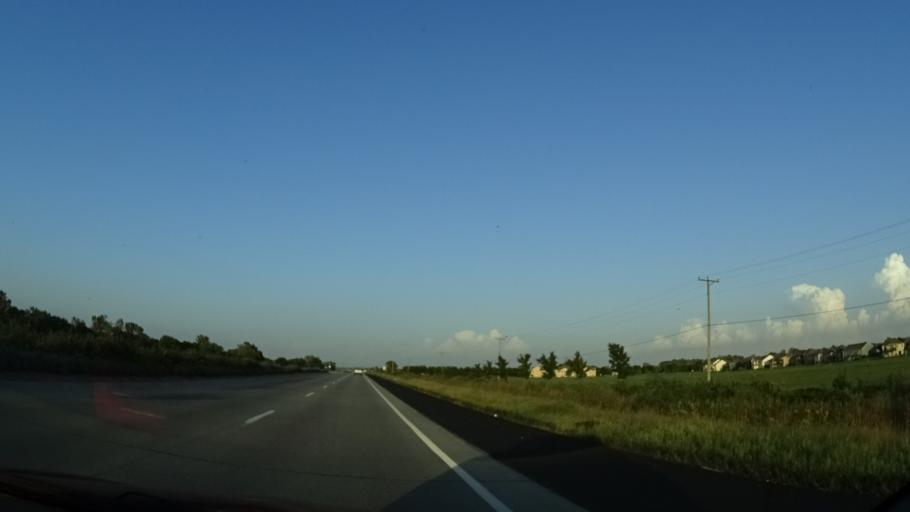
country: US
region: Nebraska
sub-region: Douglas County
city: Omaha
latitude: 41.2105
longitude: -95.9020
